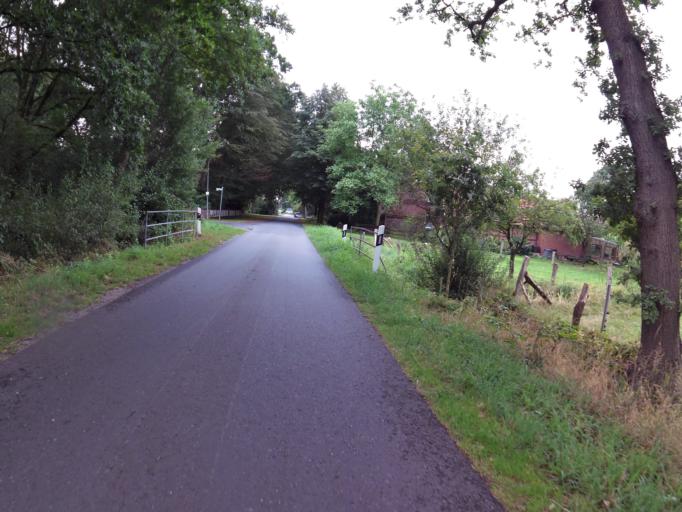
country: DE
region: Lower Saxony
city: Helvesiek
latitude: 53.1980
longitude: 9.4634
